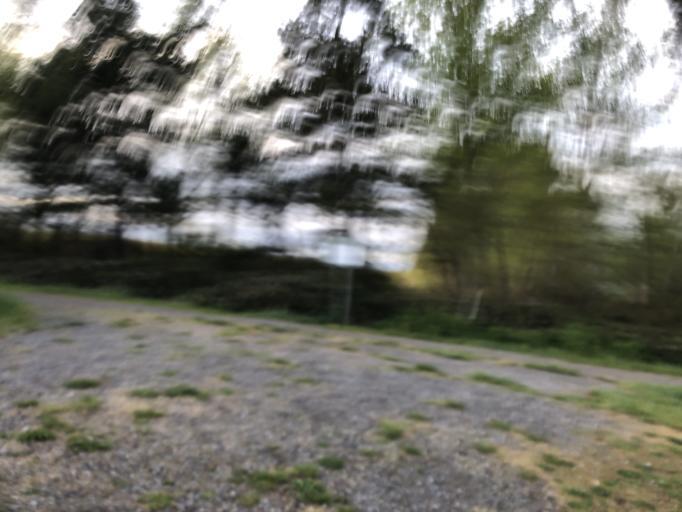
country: CA
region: British Columbia
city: Richmond
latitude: 49.1478
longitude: -123.1058
